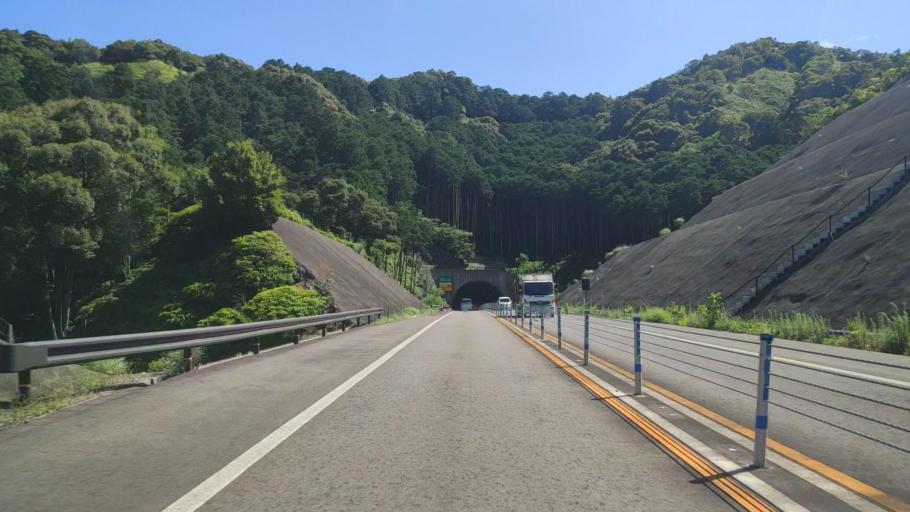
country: JP
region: Wakayama
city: Shingu
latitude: 33.6268
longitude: 135.9213
